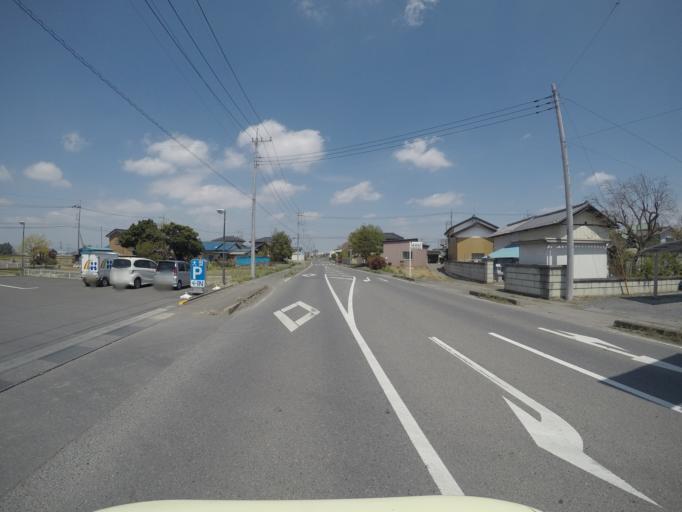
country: JP
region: Tochigi
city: Mibu
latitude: 36.3914
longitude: 139.7900
